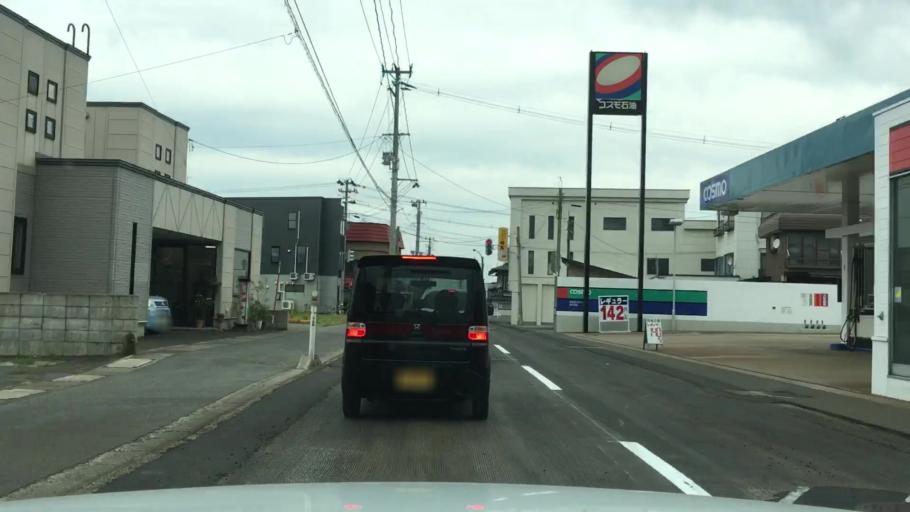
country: JP
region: Aomori
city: Hirosaki
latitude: 40.6282
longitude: 140.4540
